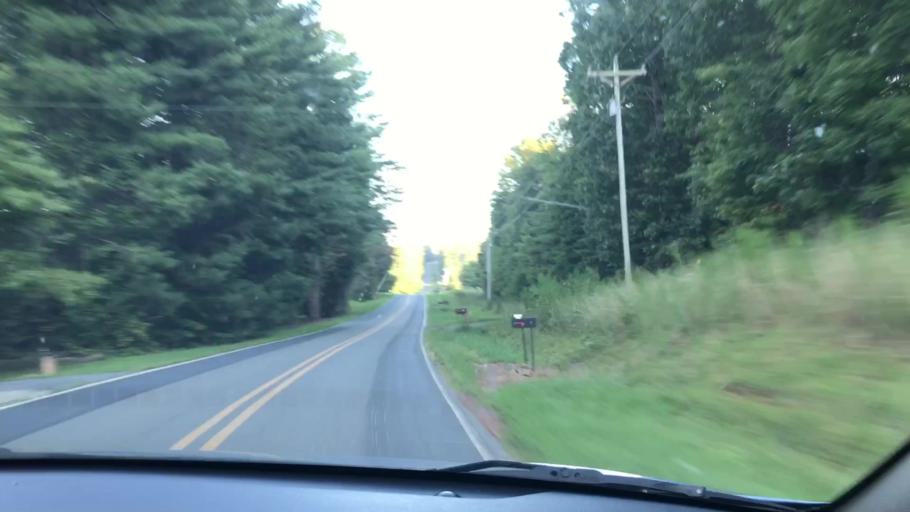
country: US
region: North Carolina
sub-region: Randolph County
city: Franklinville
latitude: 35.8110
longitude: -79.6913
